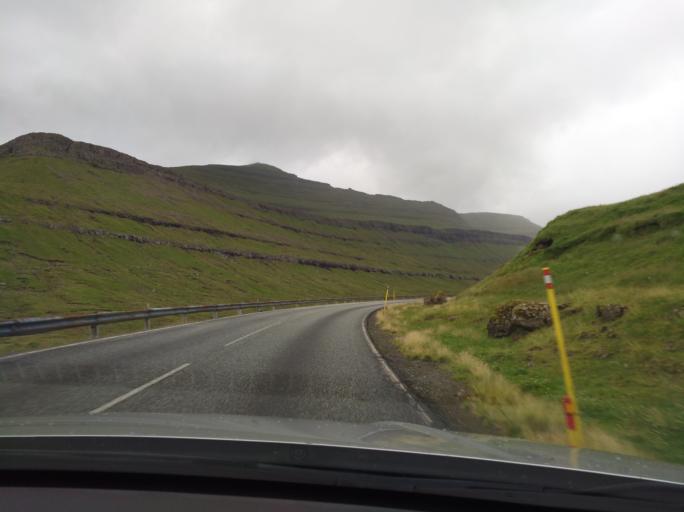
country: FO
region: Eysturoy
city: Fuglafjordur
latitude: 62.2235
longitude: -6.8793
